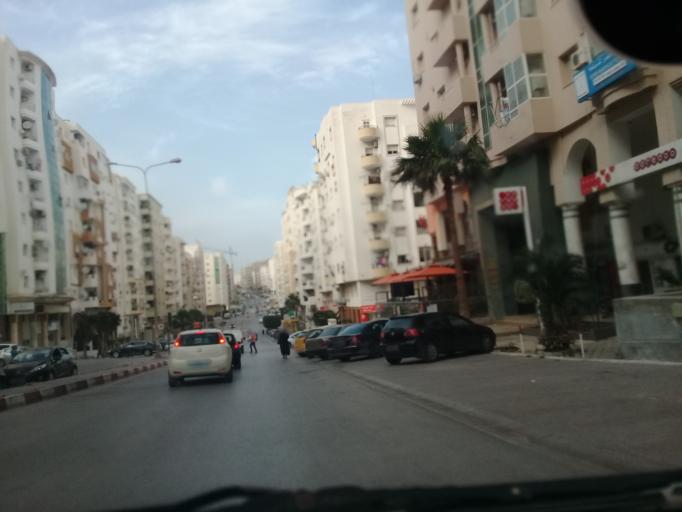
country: TN
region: Ariana
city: Ariana
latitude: 36.8639
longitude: 10.1669
